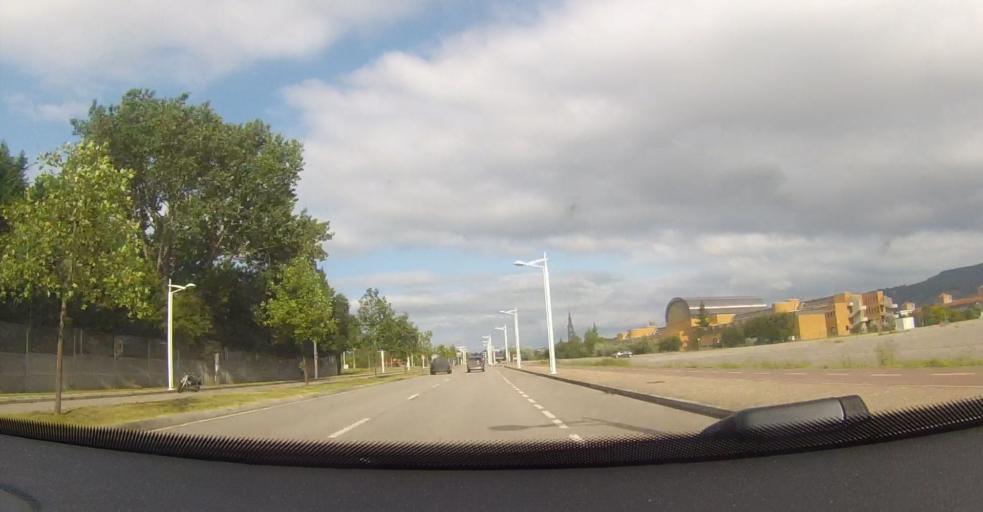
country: ES
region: Asturias
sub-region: Province of Asturias
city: Gijon
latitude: 43.5274
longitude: -5.6316
